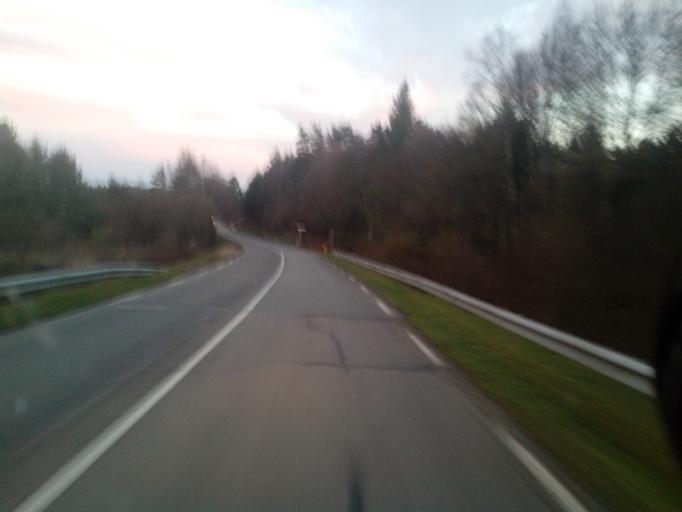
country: FR
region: Limousin
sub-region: Departement de la Correze
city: Meymac
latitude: 45.5157
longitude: 2.1772
